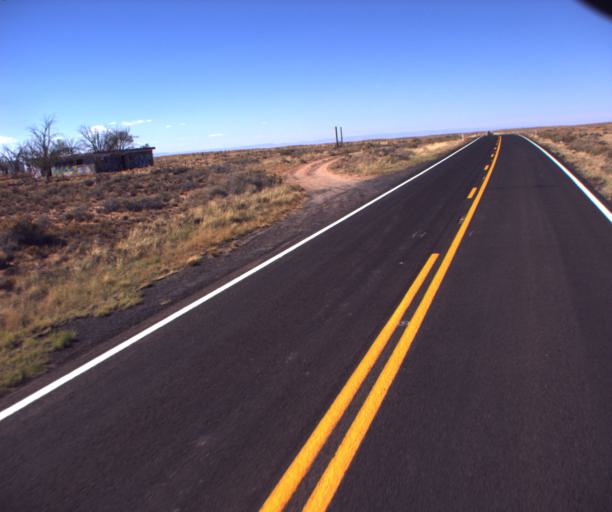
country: US
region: Arizona
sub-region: Coconino County
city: Tuba City
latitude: 35.9602
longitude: -110.9375
